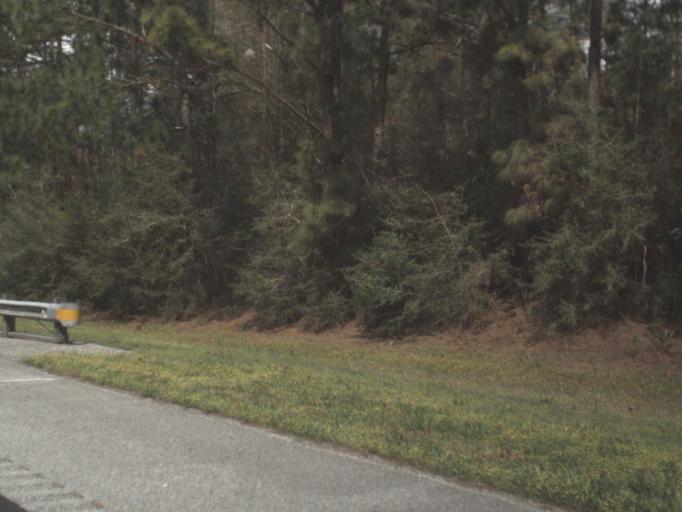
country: US
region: Florida
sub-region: Okaloosa County
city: Crestview
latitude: 30.7163
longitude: -86.6678
